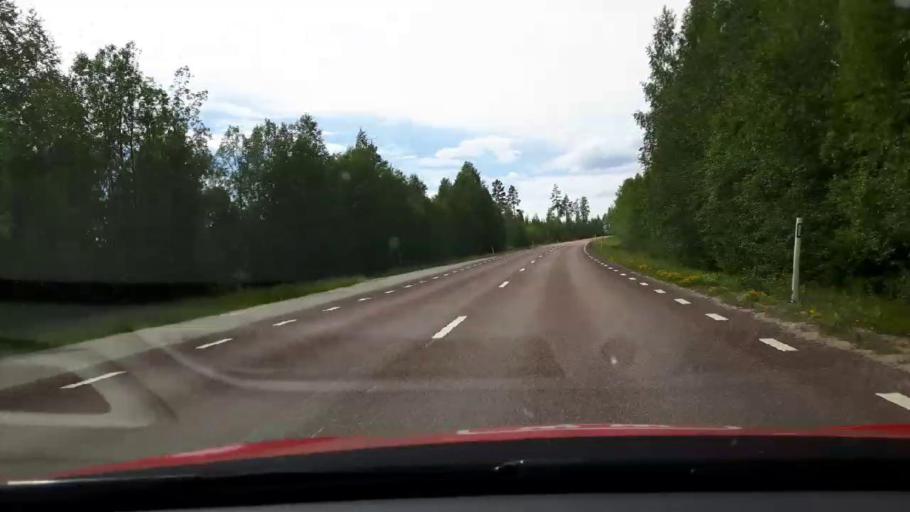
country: SE
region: Jaemtland
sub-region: Harjedalens Kommun
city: Sveg
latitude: 62.0513
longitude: 14.8965
